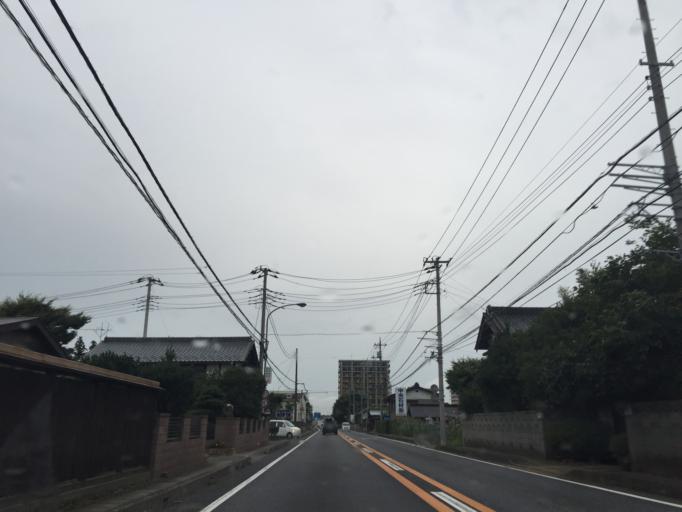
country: JP
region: Ibaraki
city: Ushiku
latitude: 36.0029
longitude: 140.1543
